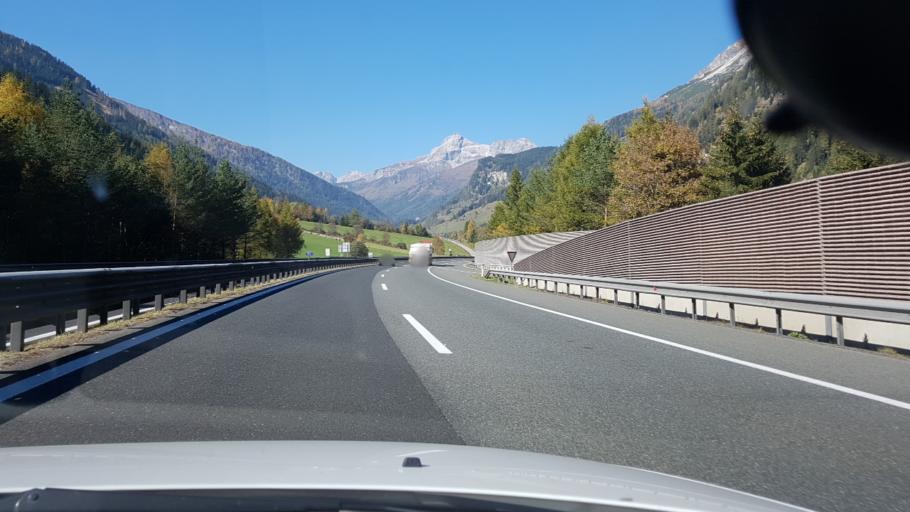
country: AT
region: Salzburg
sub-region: Politischer Bezirk Tamsweg
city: Zederhaus
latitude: 47.1591
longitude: 13.4852
